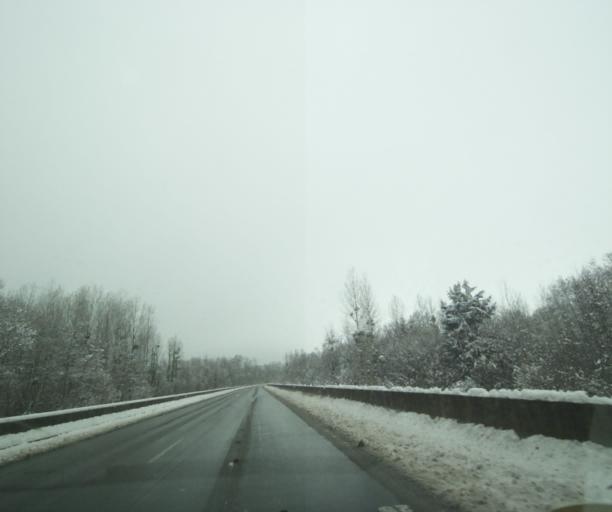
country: FR
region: Champagne-Ardenne
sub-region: Departement de la Haute-Marne
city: Villiers-en-Lieu
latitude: 48.5779
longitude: 4.8640
